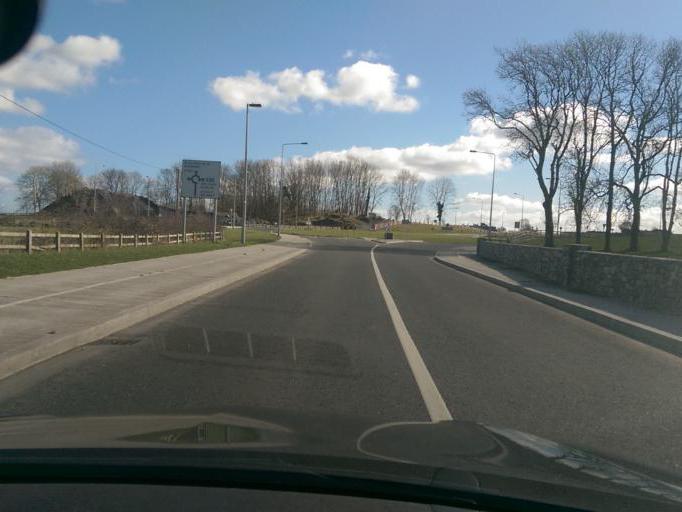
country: IE
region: Connaught
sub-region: County Galway
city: Athenry
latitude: 53.3116
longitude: -8.7561
